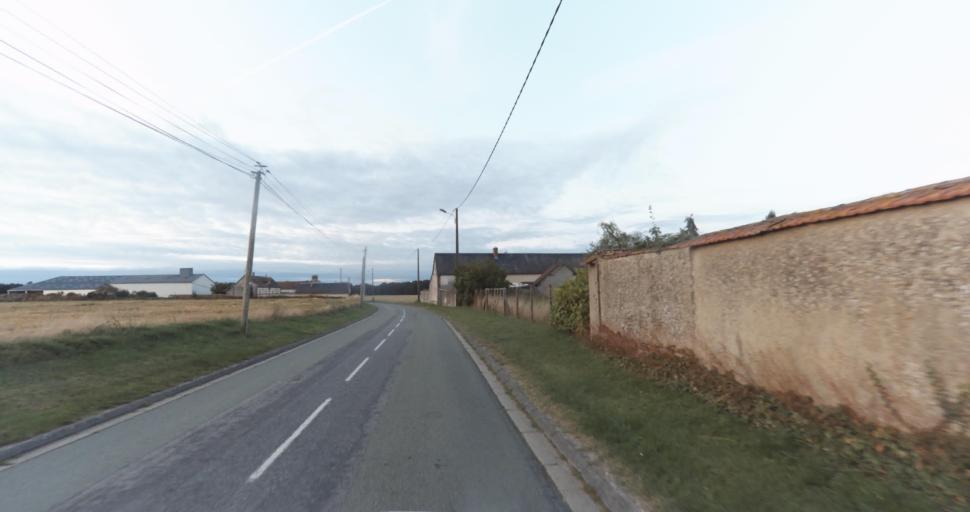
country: FR
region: Haute-Normandie
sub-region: Departement de l'Eure
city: Marcilly-sur-Eure
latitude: 48.8750
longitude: 1.2600
